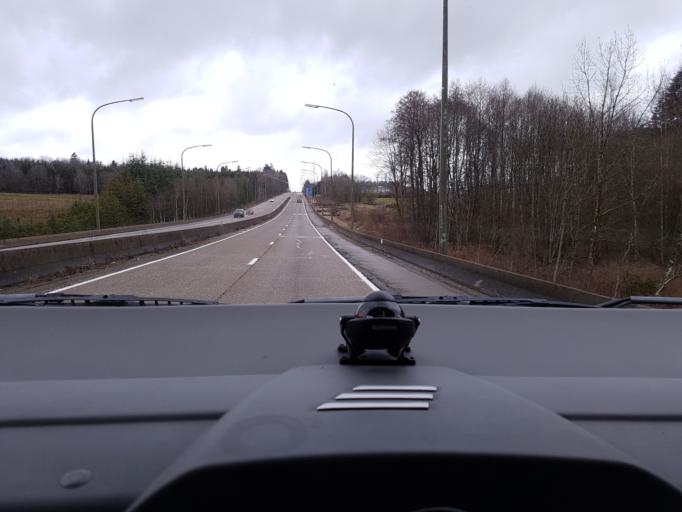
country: BE
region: Wallonia
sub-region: Province du Luxembourg
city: Tenneville
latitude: 50.0986
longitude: 5.4819
